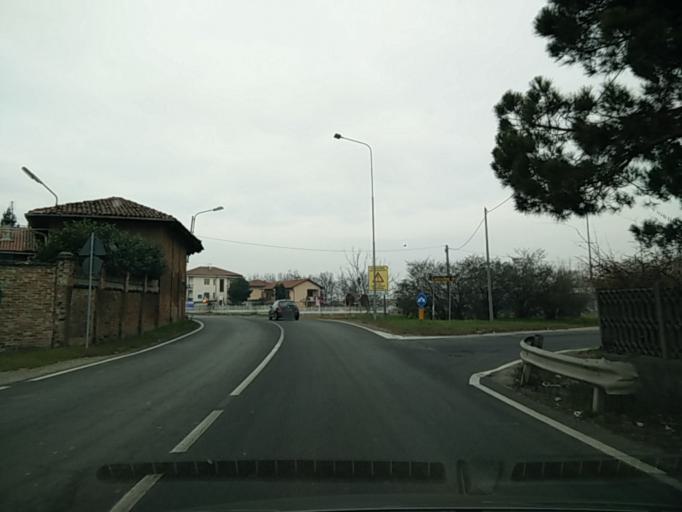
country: IT
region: Piedmont
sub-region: Provincia di Torino
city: Settimo Torinese
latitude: 45.1501
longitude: 7.7361
